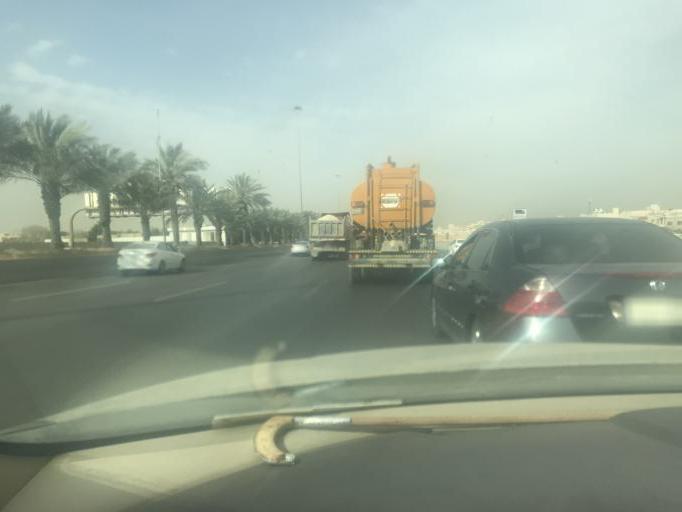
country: SA
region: Ar Riyad
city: Riyadh
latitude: 24.7907
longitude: 46.7163
